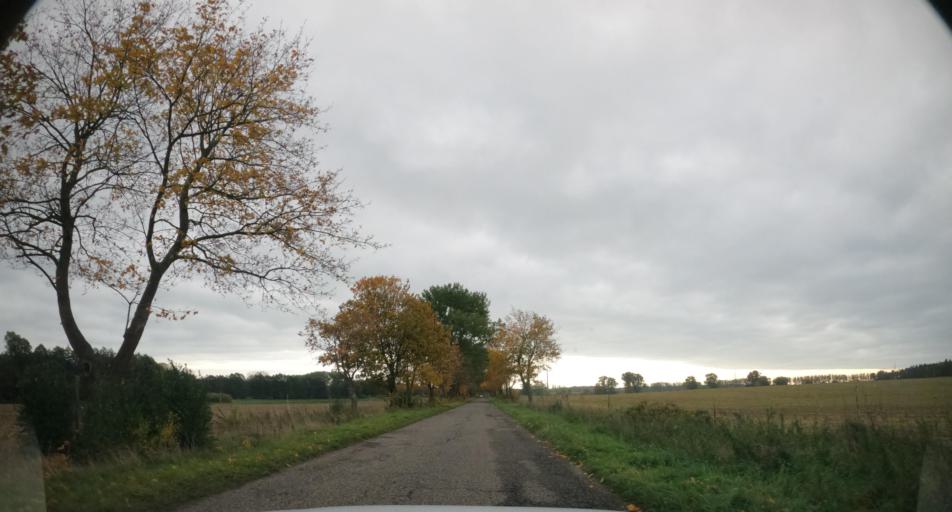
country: PL
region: West Pomeranian Voivodeship
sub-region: Powiat kamienski
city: Wolin
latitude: 53.8634
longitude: 14.5934
